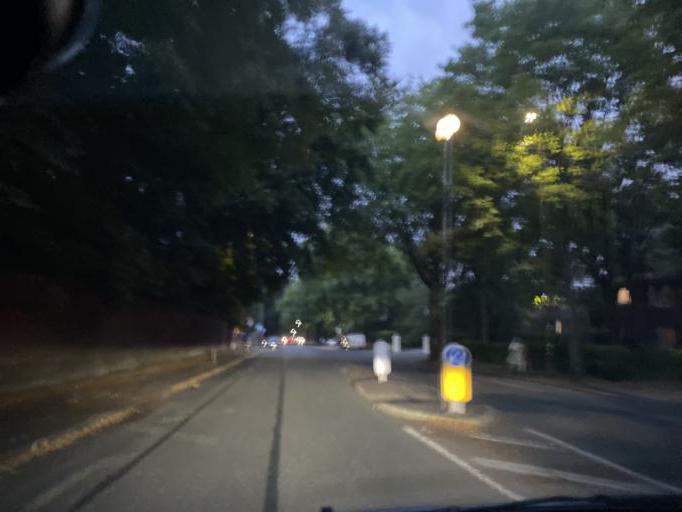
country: GB
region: England
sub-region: Manchester
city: Chorlton cum Hardy
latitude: 53.4545
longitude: -2.2653
